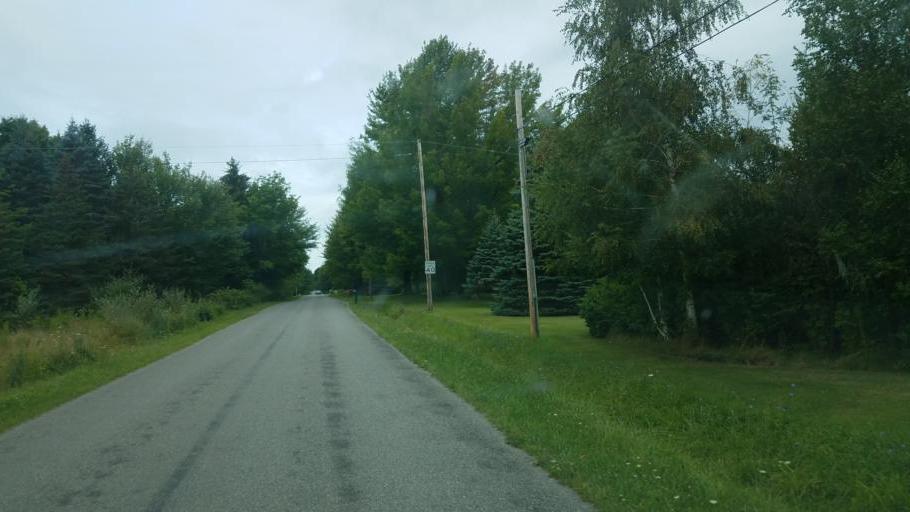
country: US
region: Pennsylvania
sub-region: Erie County
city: Lake City
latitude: 41.9944
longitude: -80.4299
